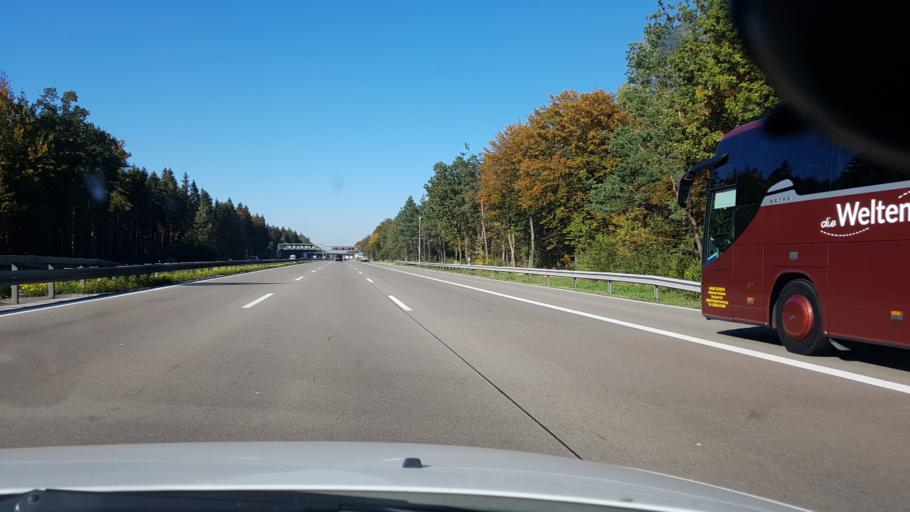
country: DE
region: Bavaria
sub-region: Upper Bavaria
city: Otterfing
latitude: 47.9331
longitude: 11.7069
